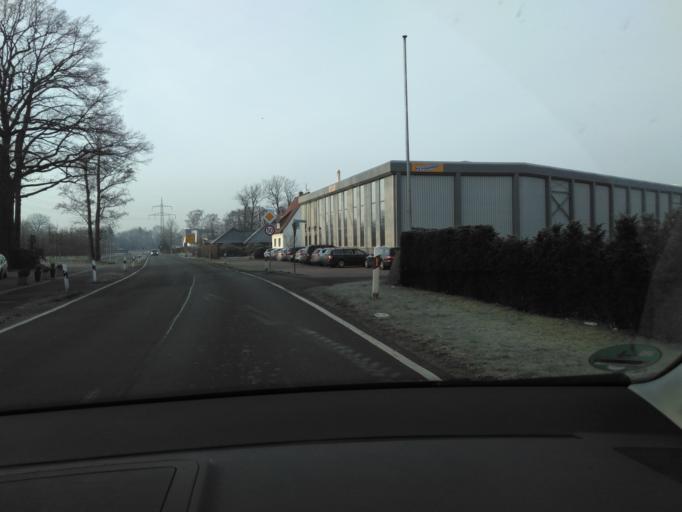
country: DE
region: North Rhine-Westphalia
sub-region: Regierungsbezirk Detmold
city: Verl
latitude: 51.8670
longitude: 8.4983
